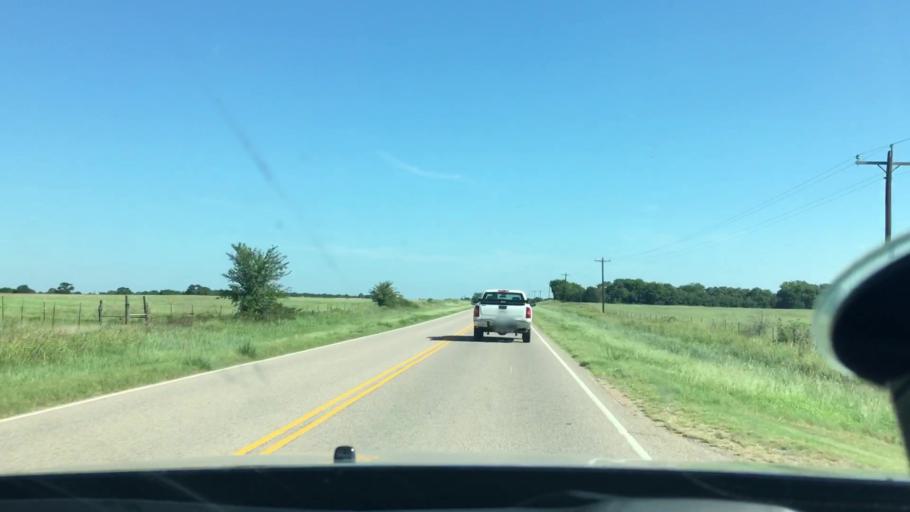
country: US
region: Oklahoma
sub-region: Johnston County
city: Tishomingo
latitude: 34.2918
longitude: -96.6710
